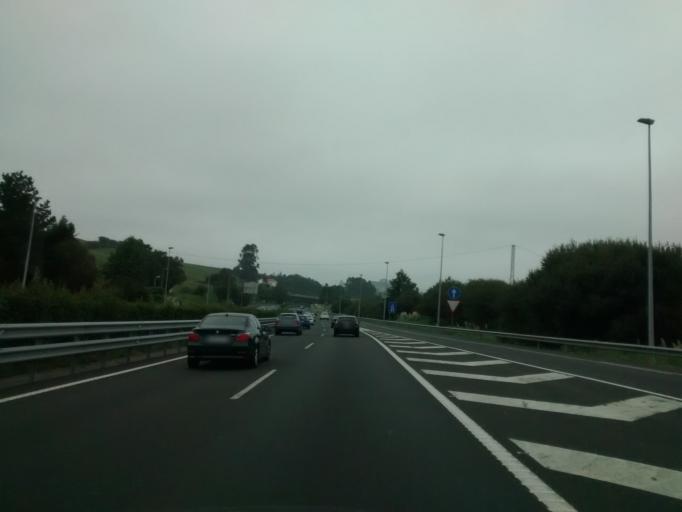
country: ES
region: Cantabria
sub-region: Provincia de Cantabria
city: Miengo
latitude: 43.4052
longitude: -3.9894
